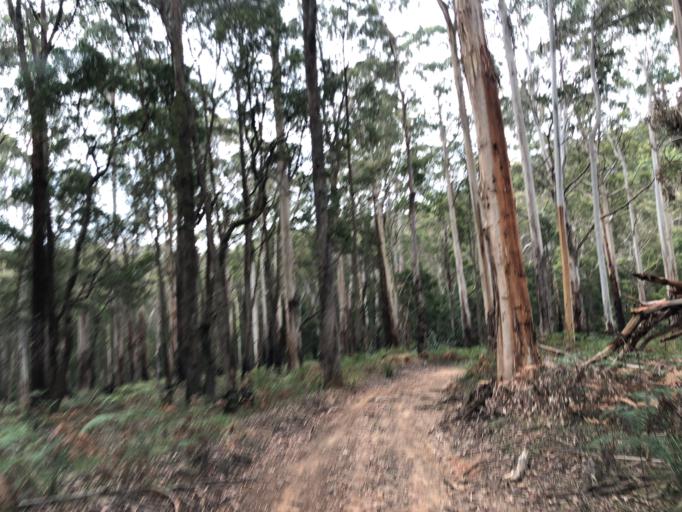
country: AU
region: Victoria
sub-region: Moorabool
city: Bacchus Marsh
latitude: -37.4407
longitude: 144.3301
